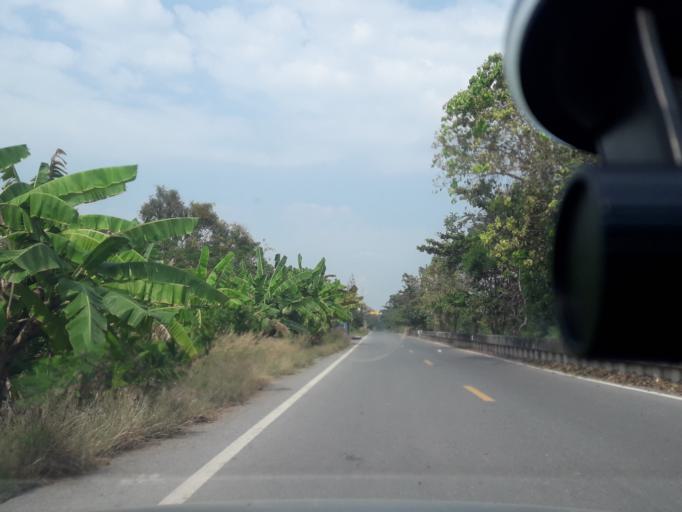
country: TH
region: Sara Buri
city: Nong Khae
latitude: 14.2424
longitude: 100.8913
